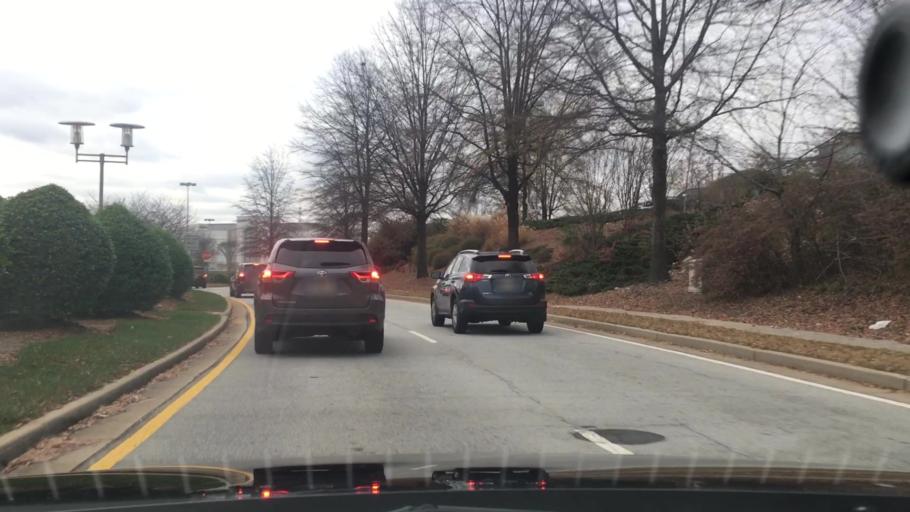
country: US
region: Georgia
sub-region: DeKalb County
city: Lithonia
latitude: 33.6982
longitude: -84.0913
